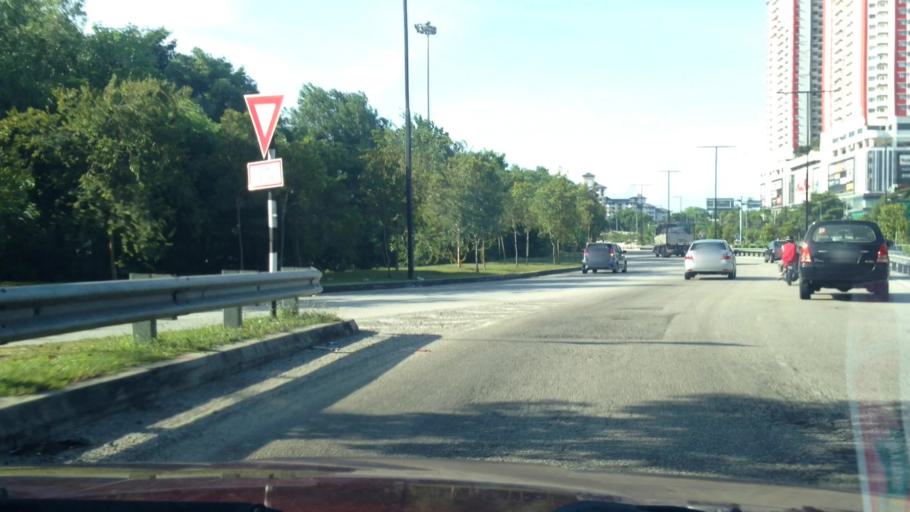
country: MY
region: Selangor
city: Subang Jaya
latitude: 3.0231
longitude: 101.5799
